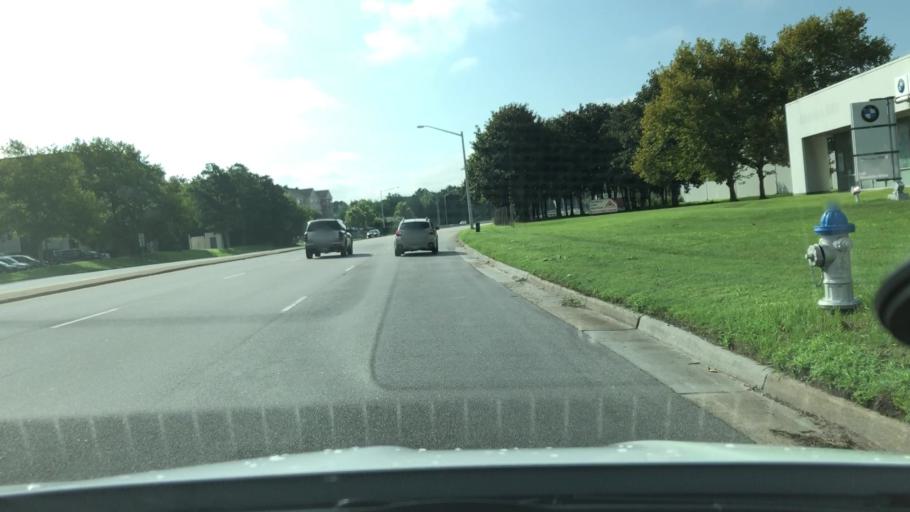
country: US
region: Virginia
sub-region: City of Chesapeake
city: Chesapeake
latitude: 36.7898
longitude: -76.2376
